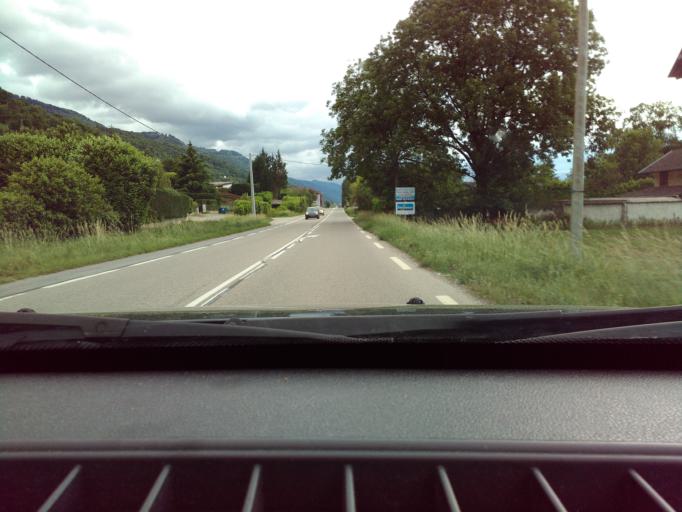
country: FR
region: Rhone-Alpes
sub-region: Departement de l'Isere
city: Le Champ-pres-Froges
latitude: 45.2885
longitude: 5.9390
